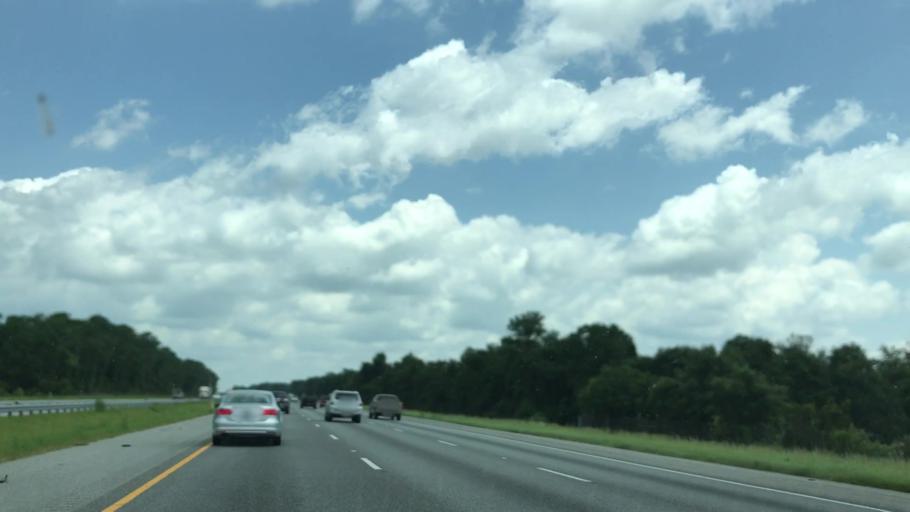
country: US
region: Georgia
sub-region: Glynn County
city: Dock Junction
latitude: 31.1720
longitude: -81.5500
